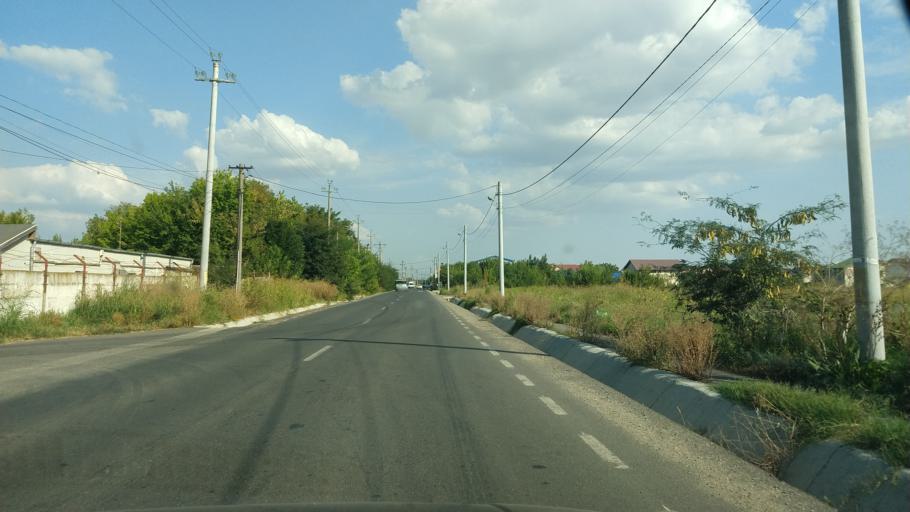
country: RO
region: Ilfov
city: Stefanestii de Jos
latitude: 44.5342
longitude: 26.2287
